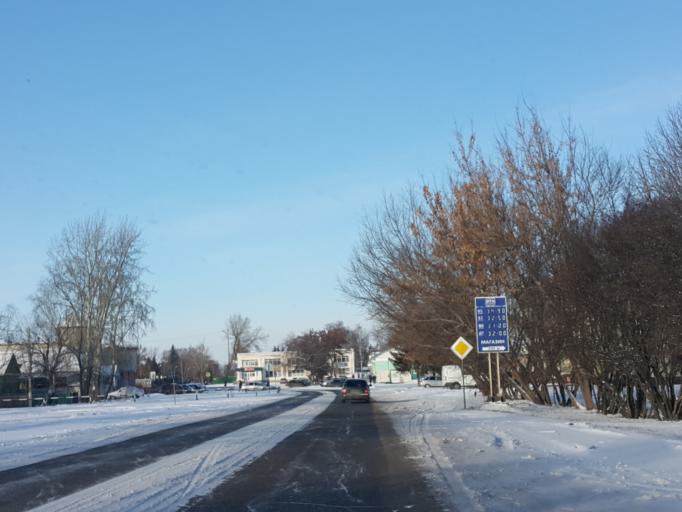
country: RU
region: Tambov
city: Znamenka
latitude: 52.4139
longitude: 41.4454
